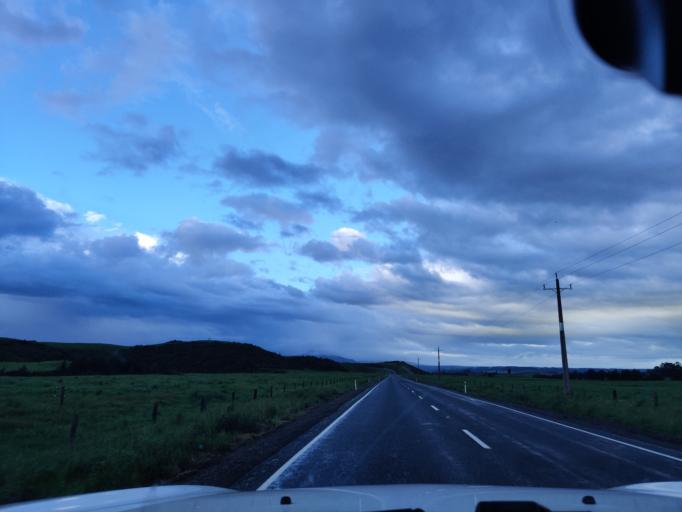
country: NZ
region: Waikato
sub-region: South Waikato District
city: Tokoroa
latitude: -38.3786
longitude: 175.7888
